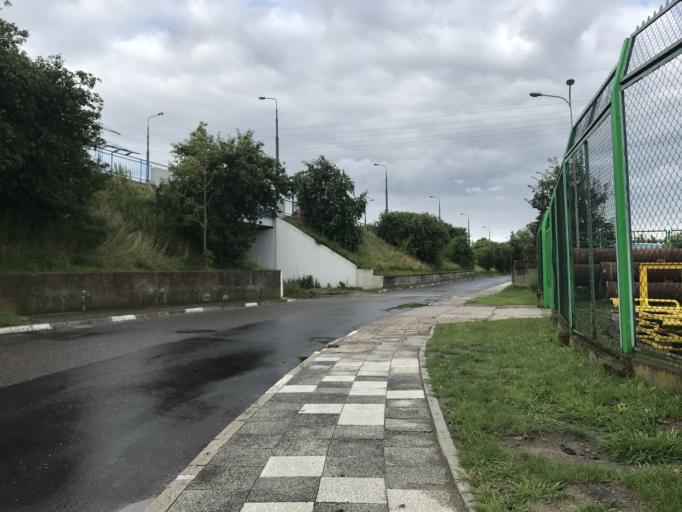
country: PL
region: Pomeranian Voivodeship
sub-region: Gdansk
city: Gdansk
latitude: 54.3546
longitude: 18.6757
